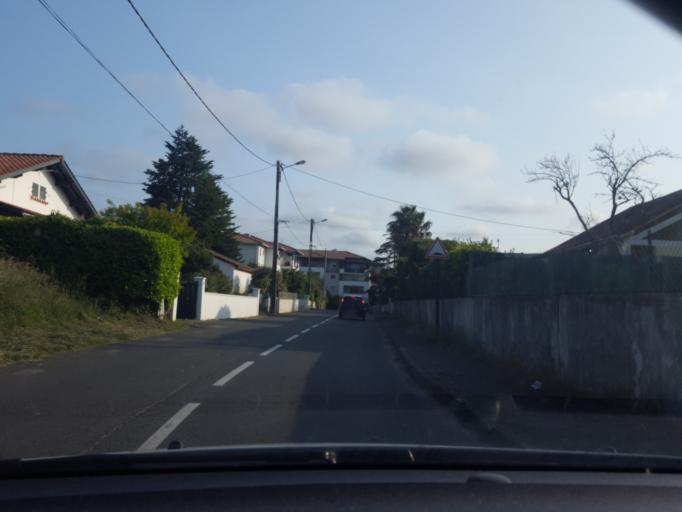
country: FR
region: Aquitaine
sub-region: Departement des Landes
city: Ondres
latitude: 43.5609
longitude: -1.4449
